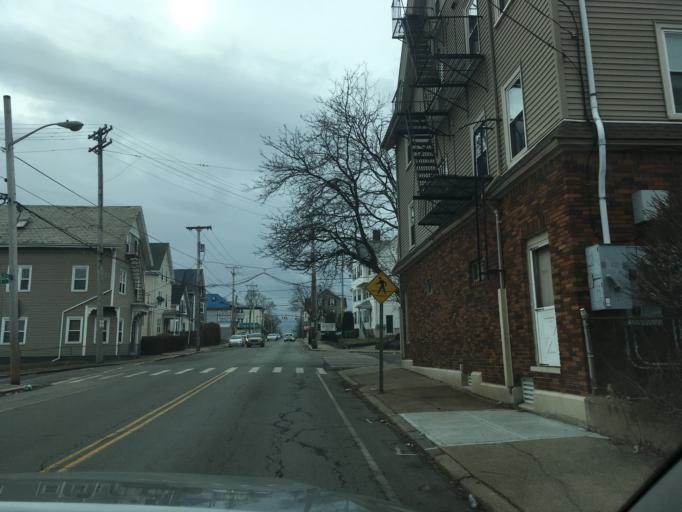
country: US
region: Rhode Island
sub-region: Providence County
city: Pawtucket
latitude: 41.8690
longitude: -71.3890
